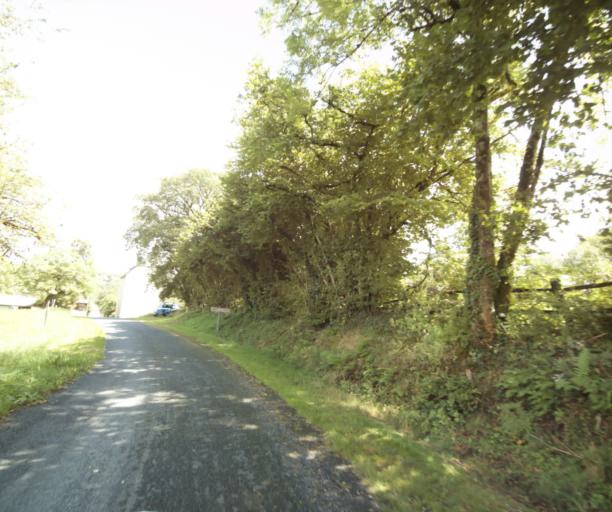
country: FR
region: Limousin
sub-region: Departement de la Correze
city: Sainte-Fortunade
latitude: 45.2045
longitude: 1.8433
